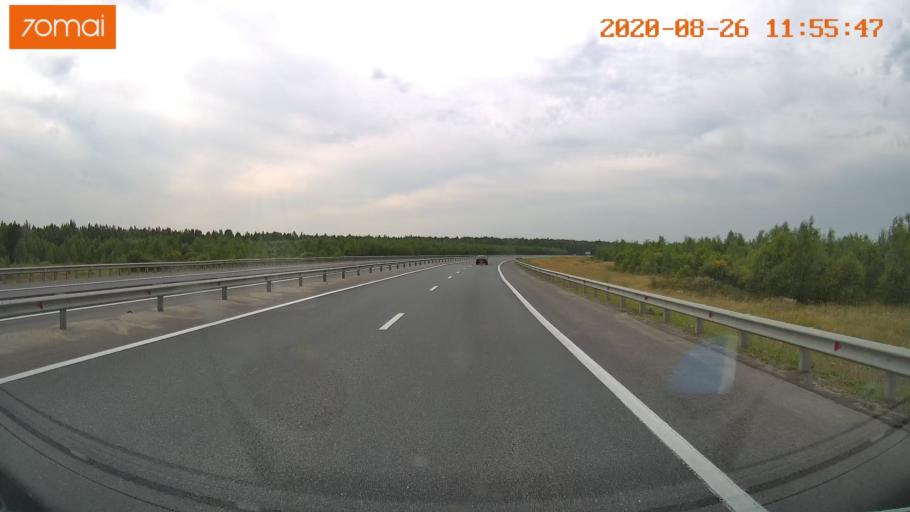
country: RU
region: Rjazan
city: Kiritsy
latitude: 54.2688
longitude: 40.3905
